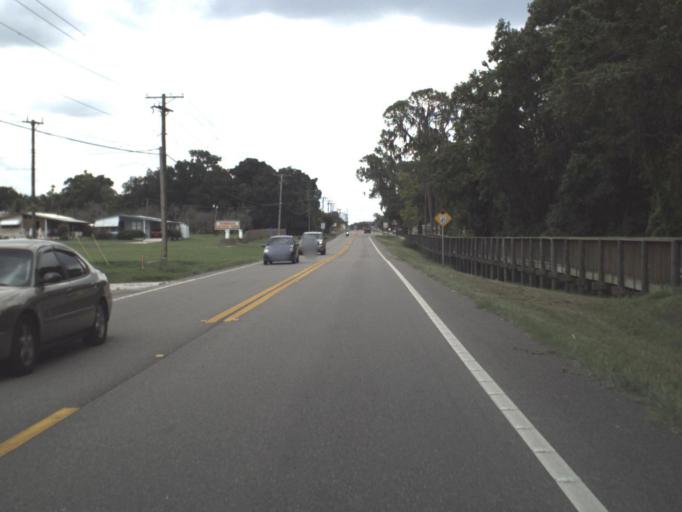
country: US
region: Florida
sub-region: Hillsborough County
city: Plant City
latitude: 28.0200
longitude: -82.1670
